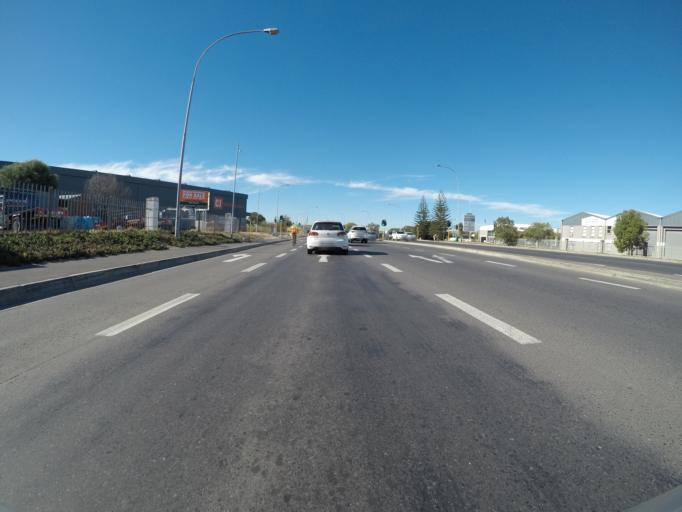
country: ZA
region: Western Cape
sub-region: City of Cape Town
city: Kraaifontein
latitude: -33.8963
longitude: 18.6717
